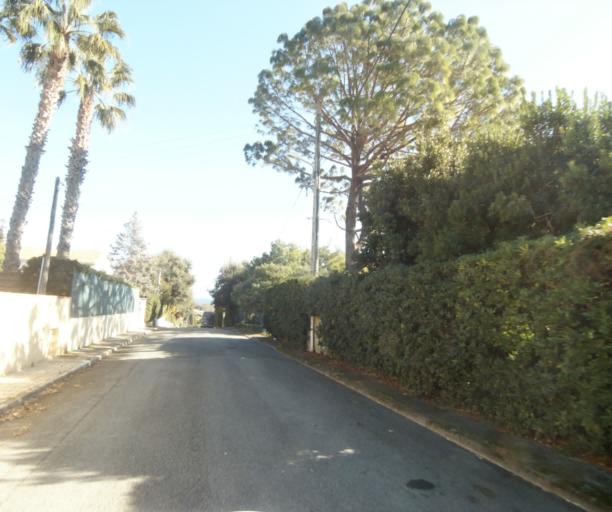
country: FR
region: Provence-Alpes-Cote d'Azur
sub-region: Departement des Alpes-Maritimes
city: Biot
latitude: 43.6197
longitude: 7.1212
